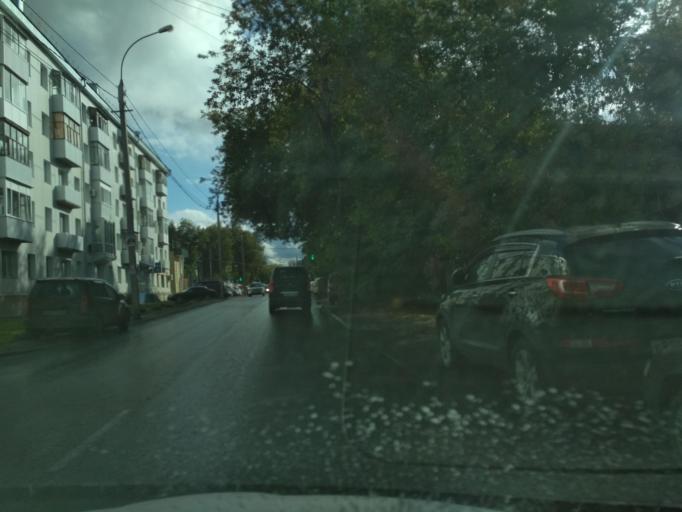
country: RU
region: Tomsk
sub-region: Tomskiy Rayon
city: Tomsk
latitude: 56.4674
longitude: 84.9756
